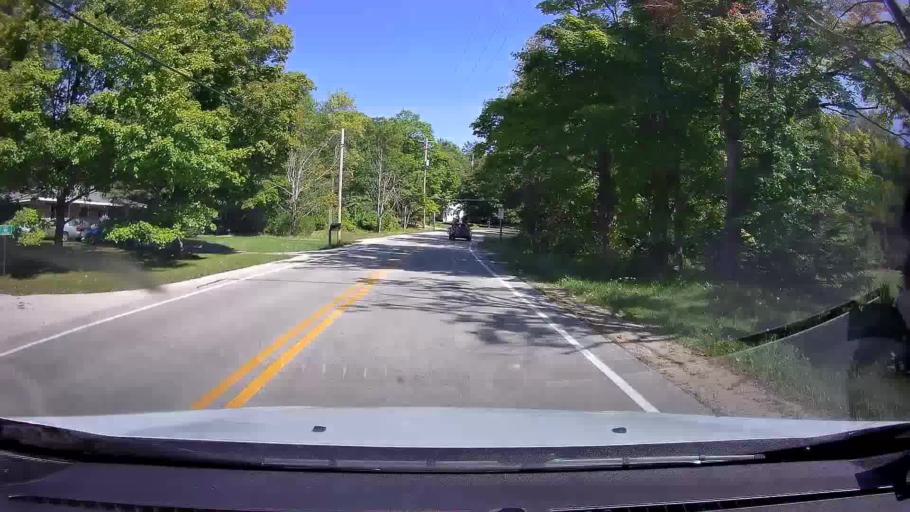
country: US
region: Michigan
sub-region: Delta County
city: Escanaba
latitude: 45.2905
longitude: -87.0195
